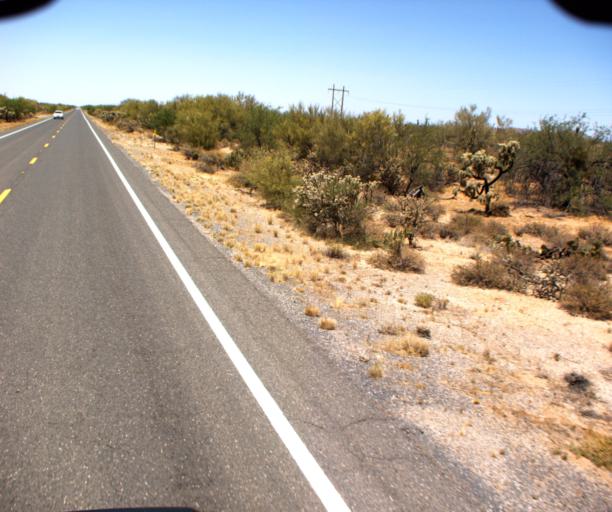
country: US
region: Arizona
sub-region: Pinal County
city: Florence
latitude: 32.8286
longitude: -111.2098
